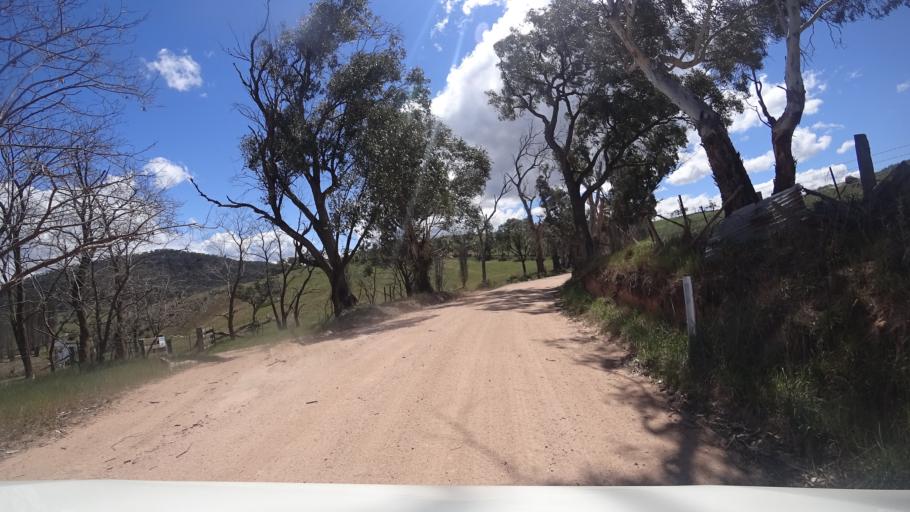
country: AU
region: New South Wales
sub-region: Oberon
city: Oberon
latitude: -33.5646
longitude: 149.9405
